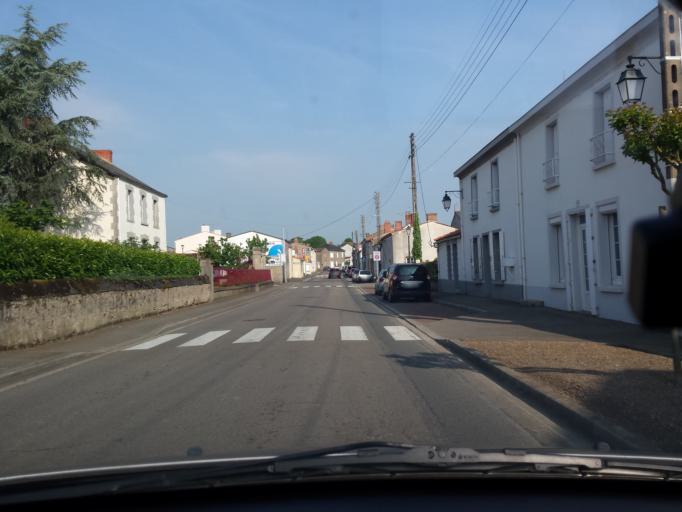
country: FR
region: Pays de la Loire
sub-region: Departement de la Loire-Atlantique
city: Touvois
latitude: 46.9014
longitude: -1.6808
